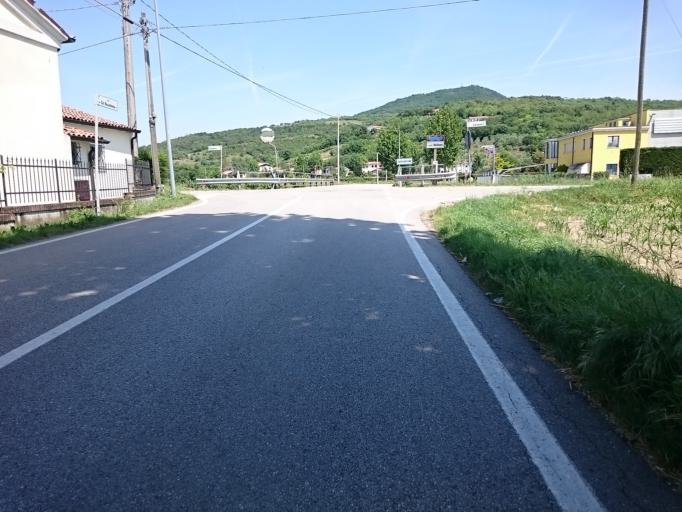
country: IT
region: Veneto
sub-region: Provincia di Padova
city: Lozzo Atestino
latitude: 45.2789
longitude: 11.6161
